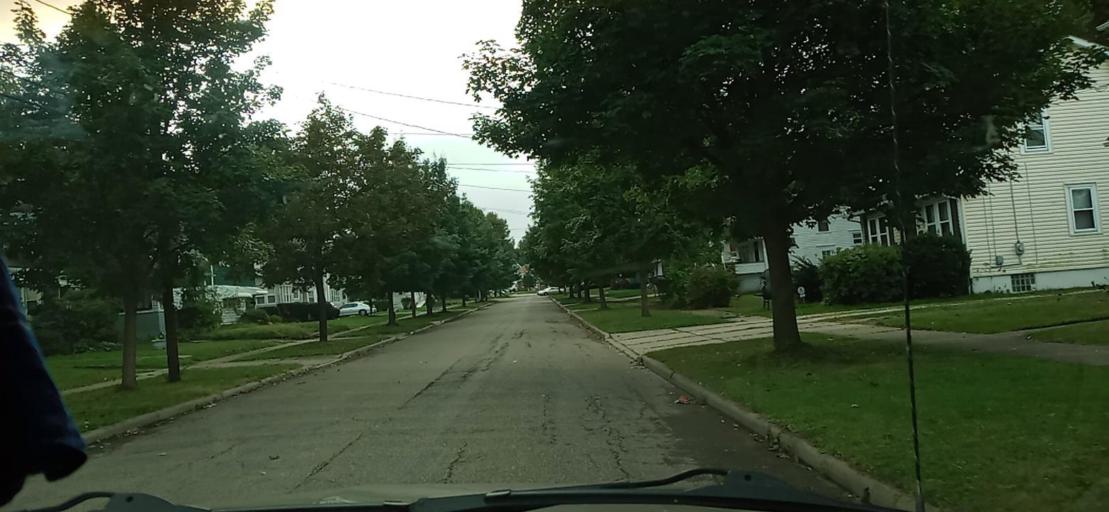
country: US
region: Ohio
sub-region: Summit County
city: Akron
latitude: 41.0809
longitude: -81.5507
